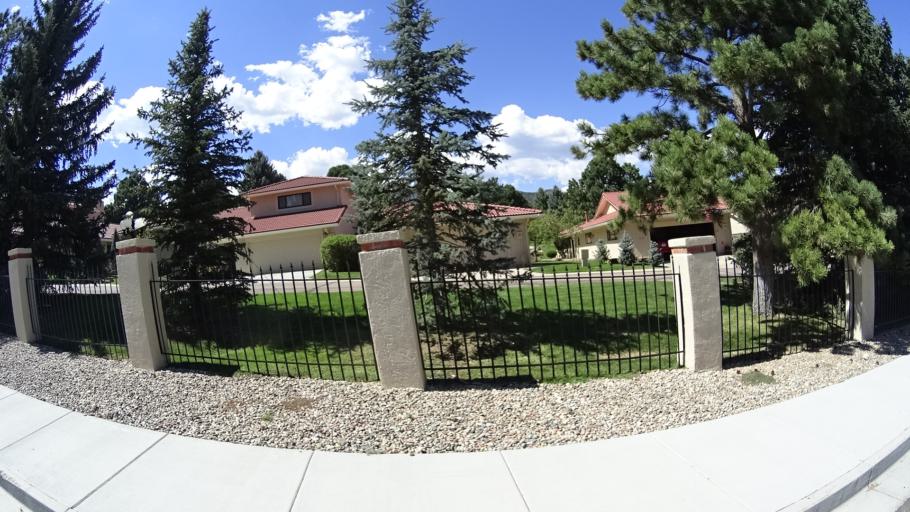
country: US
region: Colorado
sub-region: El Paso County
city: Colorado Springs
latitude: 38.7863
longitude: -104.8554
